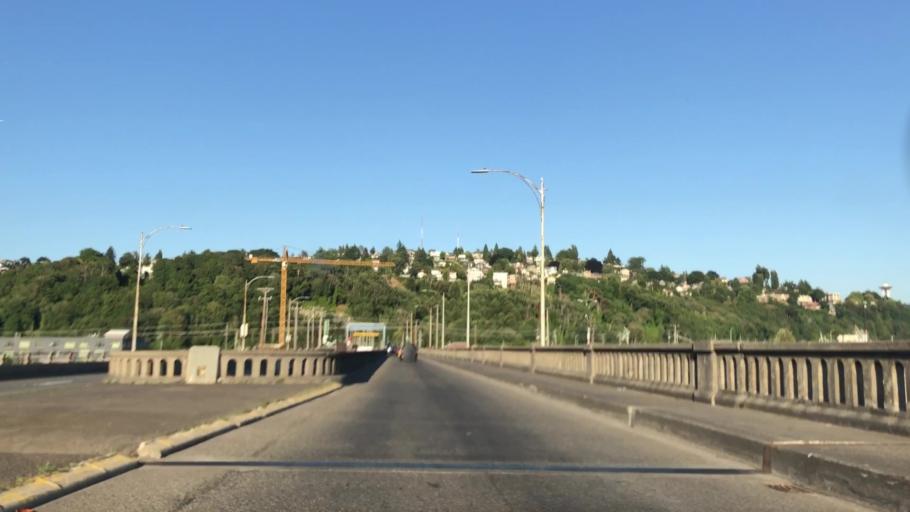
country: US
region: Washington
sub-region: King County
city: Seattle
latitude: 47.6334
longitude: -122.3819
